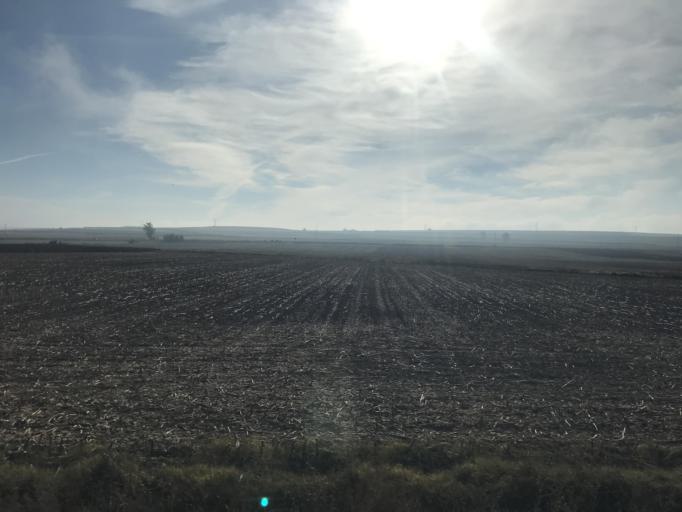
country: ES
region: Castille and Leon
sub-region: Provincia de Burgos
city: Grisalena
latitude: 42.5961
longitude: -3.2914
